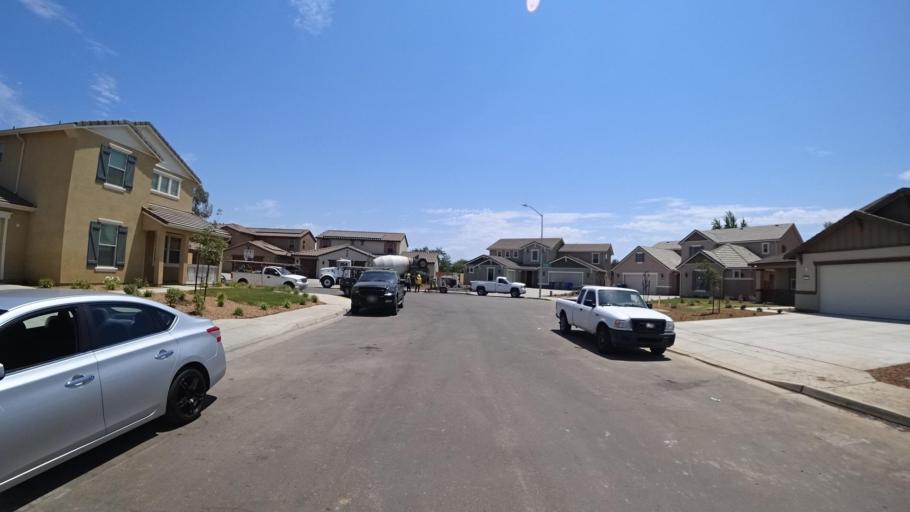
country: US
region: California
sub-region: Fresno County
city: Tarpey Village
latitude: 36.7744
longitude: -119.6570
